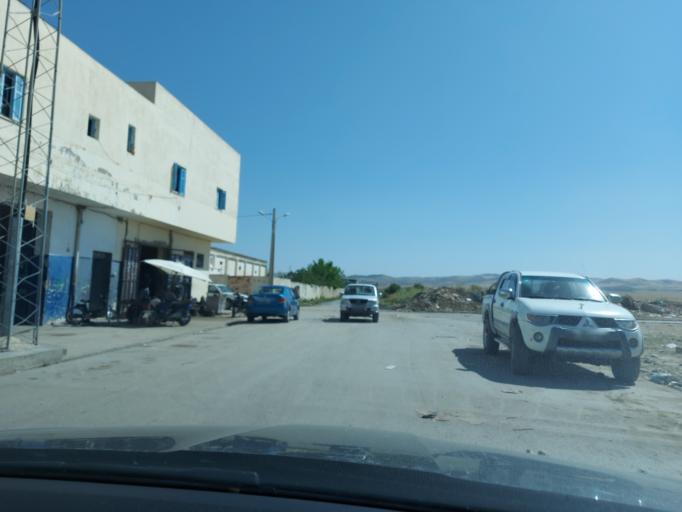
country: TN
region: Silyanah
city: Siliana
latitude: 36.0910
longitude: 9.3774
